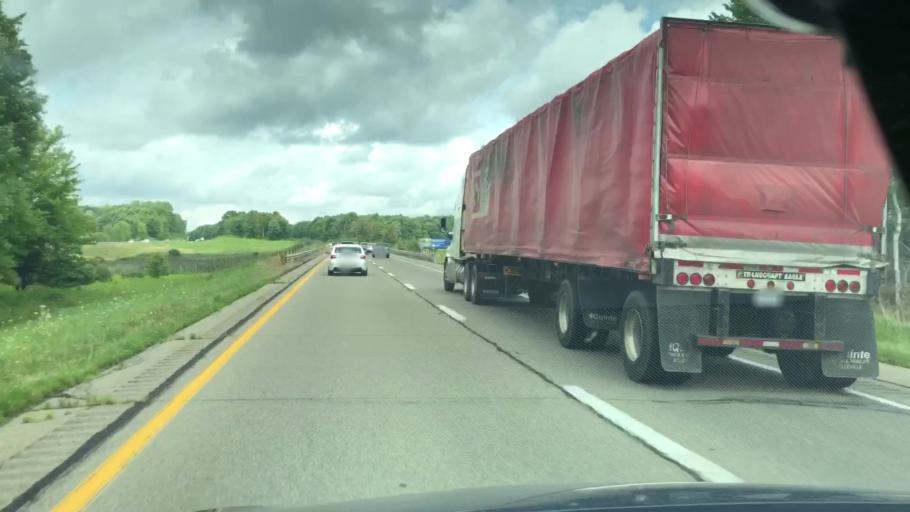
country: US
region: Pennsylvania
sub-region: Erie County
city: Edinboro
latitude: 41.7799
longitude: -80.1826
